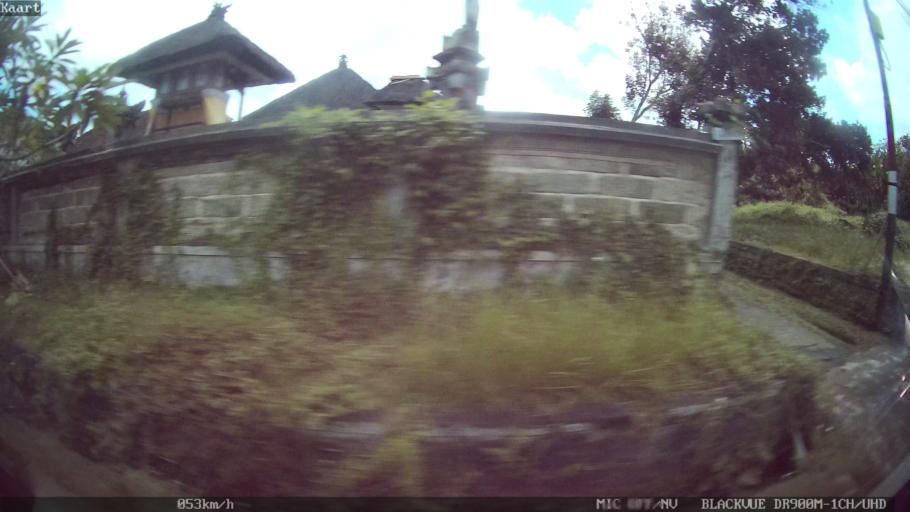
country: ID
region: Bali
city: Banjar Sedang
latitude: -8.5595
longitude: 115.2866
